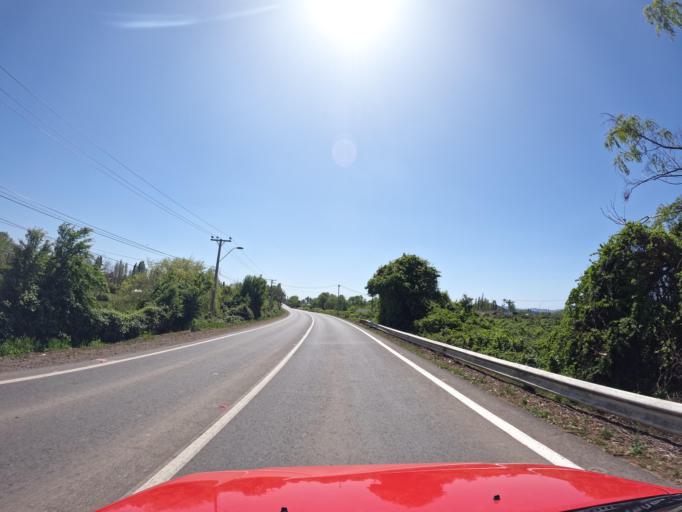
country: CL
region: Maule
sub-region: Provincia de Linares
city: Colbun
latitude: -35.7519
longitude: -71.4177
